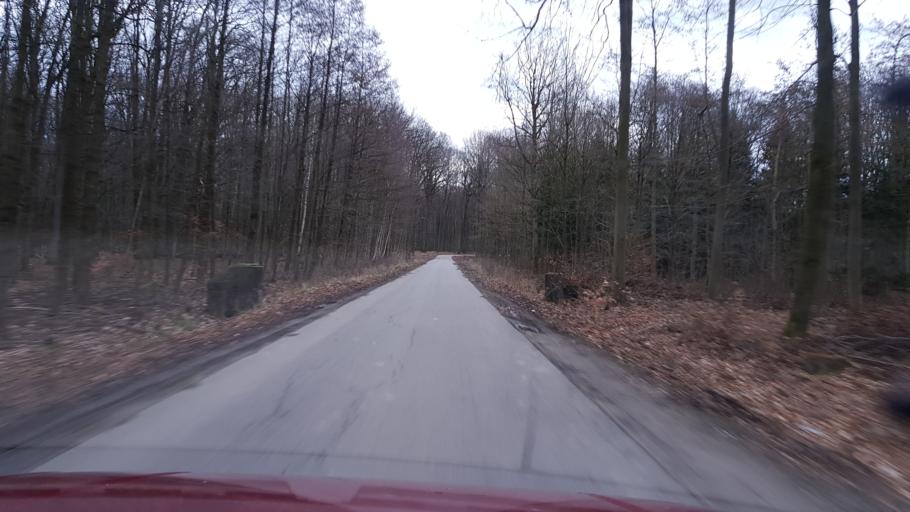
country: PL
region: West Pomeranian Voivodeship
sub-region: Powiat gryfinski
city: Stare Czarnowo
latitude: 53.3149
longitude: 14.7143
